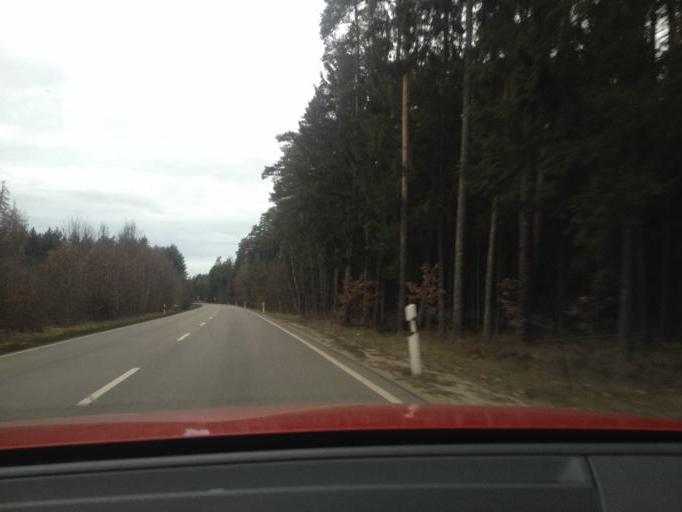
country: DE
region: Bavaria
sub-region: Regierungsbezirk Mittelfranken
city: Heilsbronn
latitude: 49.3186
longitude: 10.7926
